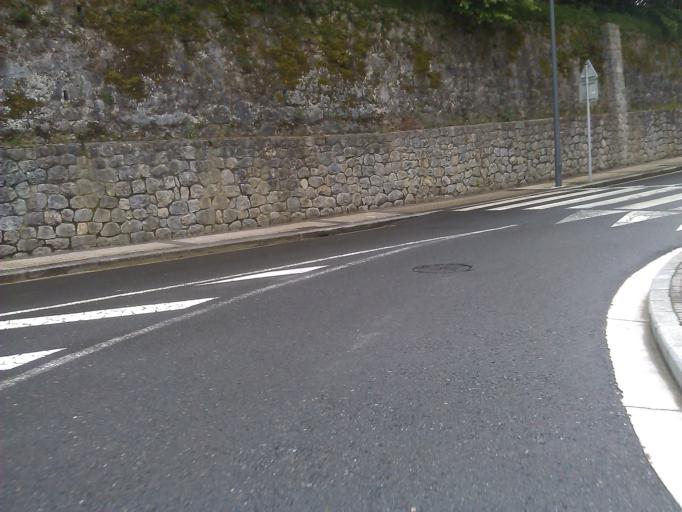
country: ES
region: Basque Country
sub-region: Provincia de Guipuzcoa
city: Andoain
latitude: 43.2218
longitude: -2.0150
